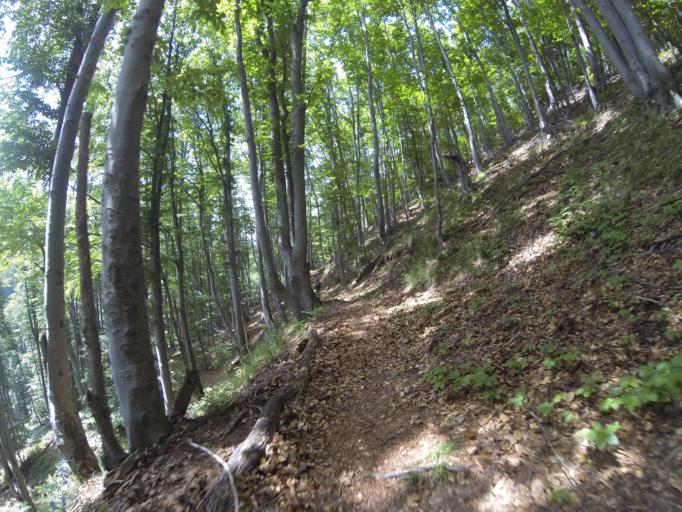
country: RO
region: Valcea
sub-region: Oras Baile Olanesti
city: Cheia
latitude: 45.2279
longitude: 24.1862
